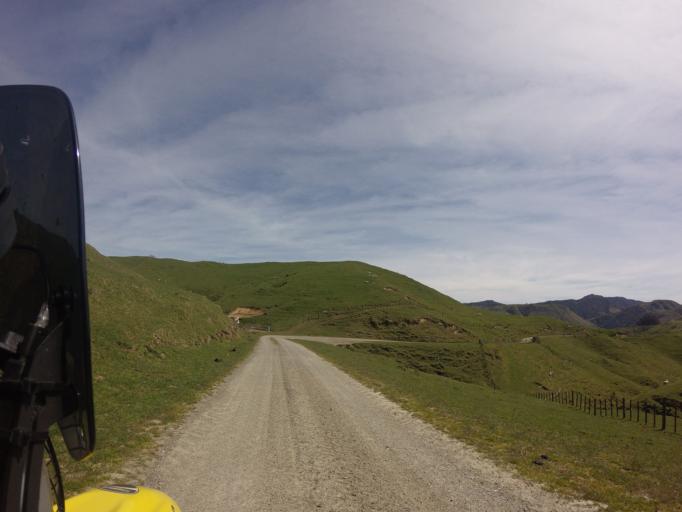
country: NZ
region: Bay of Plenty
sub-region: Opotiki District
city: Opotiki
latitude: -38.4542
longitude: 177.3598
